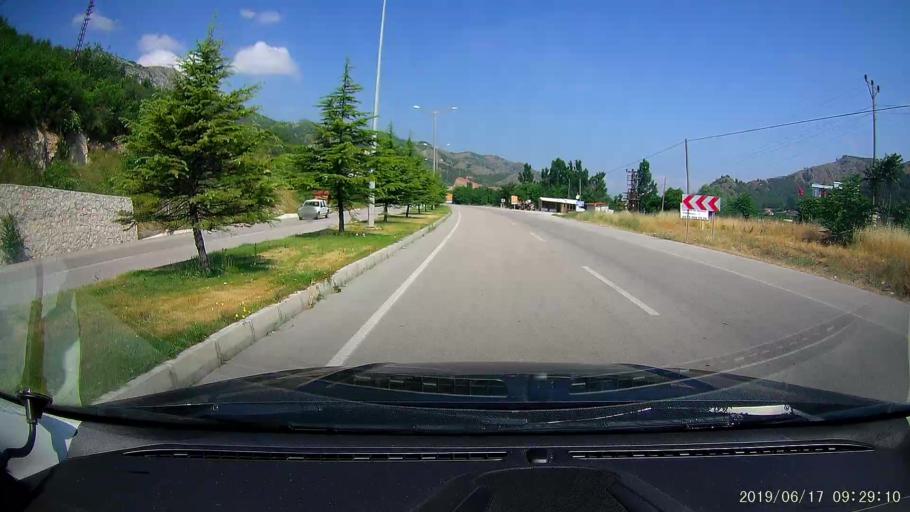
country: TR
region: Amasya
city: Amasya
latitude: 40.6947
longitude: 35.8154
